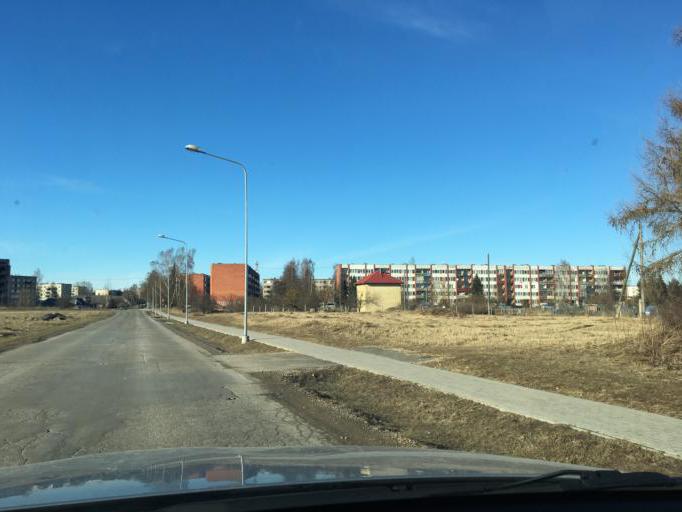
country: LV
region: Jekabpils Rajons
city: Jekabpils
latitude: 56.4866
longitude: 25.8665
